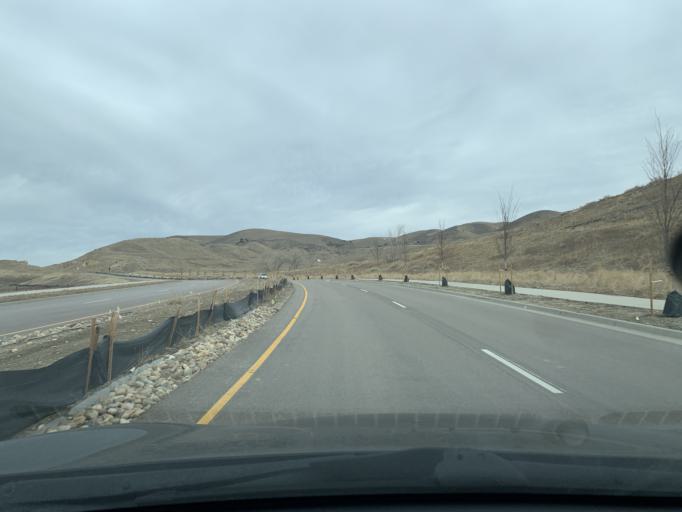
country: US
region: Colorado
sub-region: Jefferson County
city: West Pleasant View
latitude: 39.6809
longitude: -105.1831
